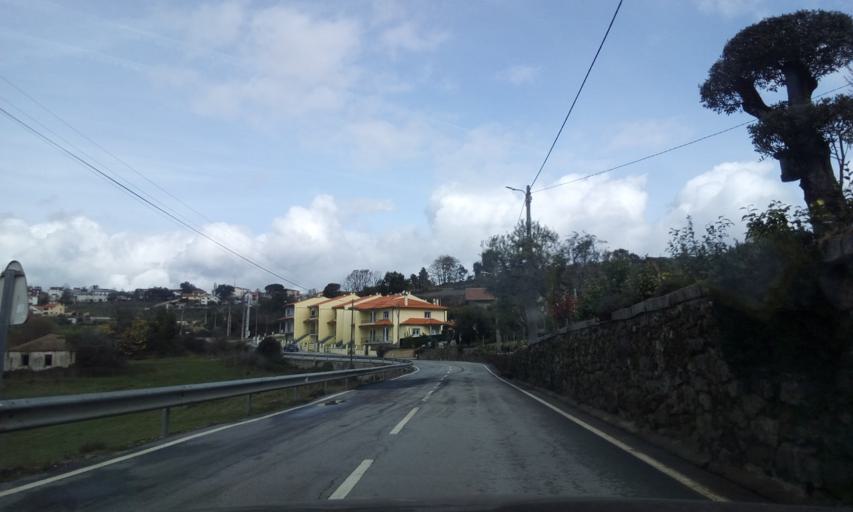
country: PT
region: Viseu
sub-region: Satao
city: Satao
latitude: 40.6691
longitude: -7.6934
